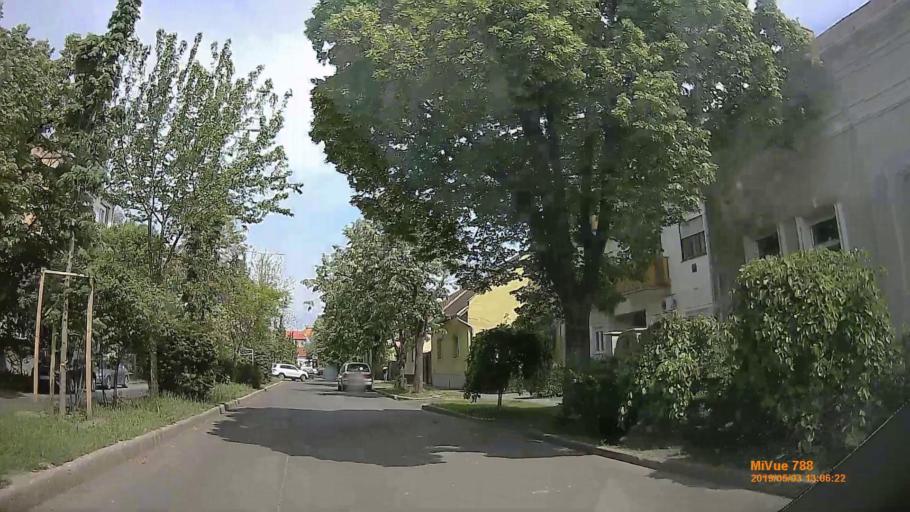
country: HU
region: Jasz-Nagykun-Szolnok
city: Szolnok
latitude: 47.1751
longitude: 20.1805
